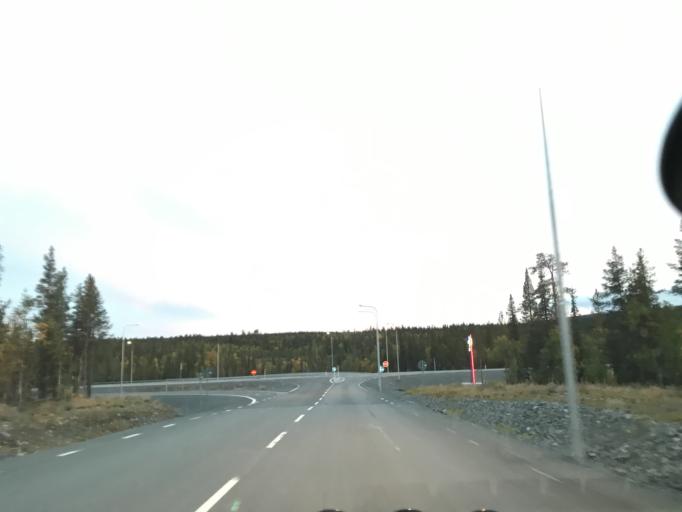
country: SE
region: Norrbotten
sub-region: Gallivare Kommun
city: Malmberget
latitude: 67.6957
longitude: 20.8099
